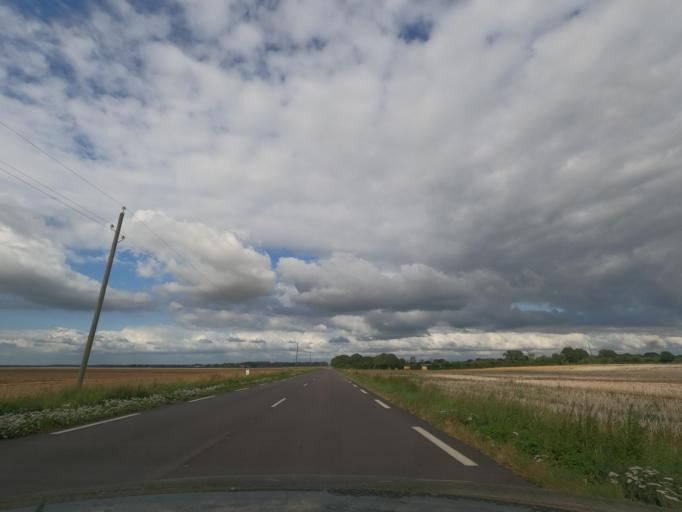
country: FR
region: Lower Normandy
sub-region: Departement du Calvados
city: Orbec
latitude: 48.9229
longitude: 0.4320
